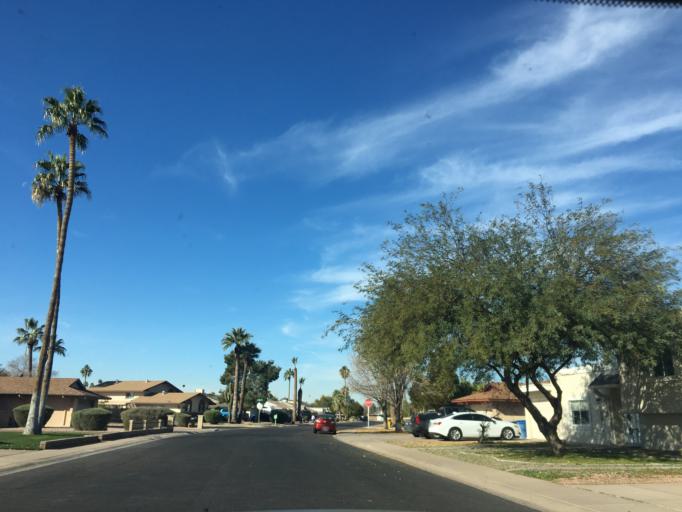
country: US
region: Arizona
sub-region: Maricopa County
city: Tempe
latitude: 33.3889
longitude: -111.9129
